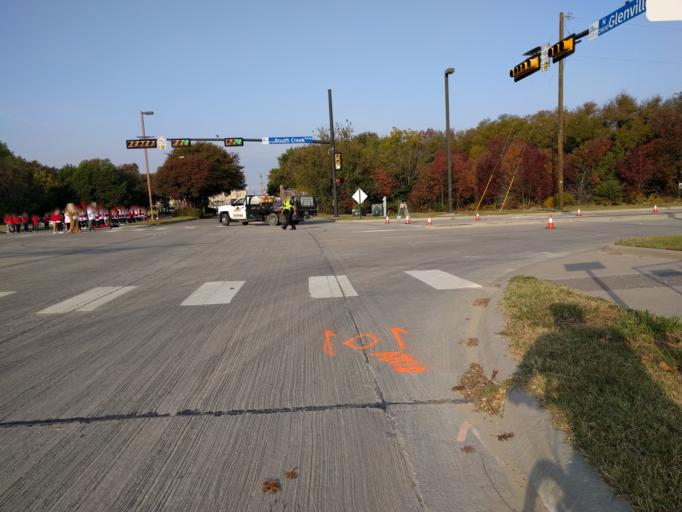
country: US
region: Texas
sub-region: Collin County
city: Plano
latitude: 32.9906
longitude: -96.7067
